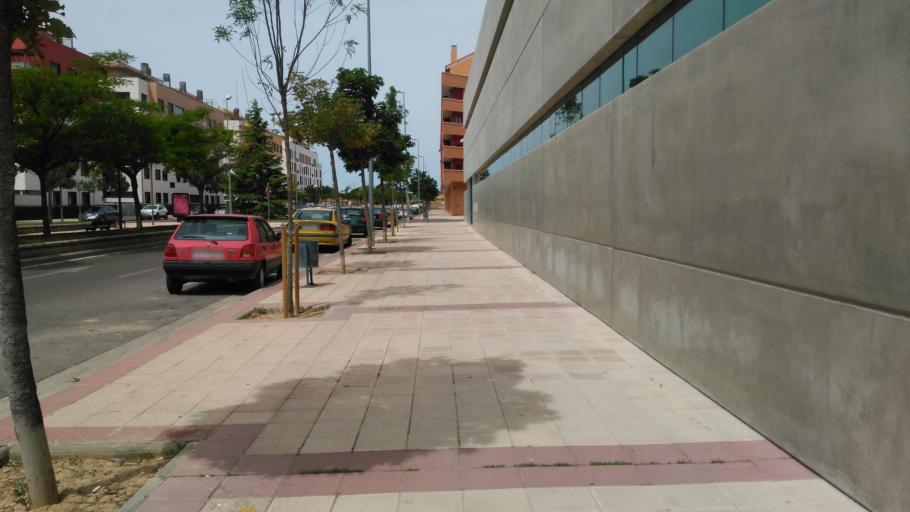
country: ES
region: Aragon
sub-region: Provincia de Huesca
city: Huesca
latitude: 42.1435
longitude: -0.4187
